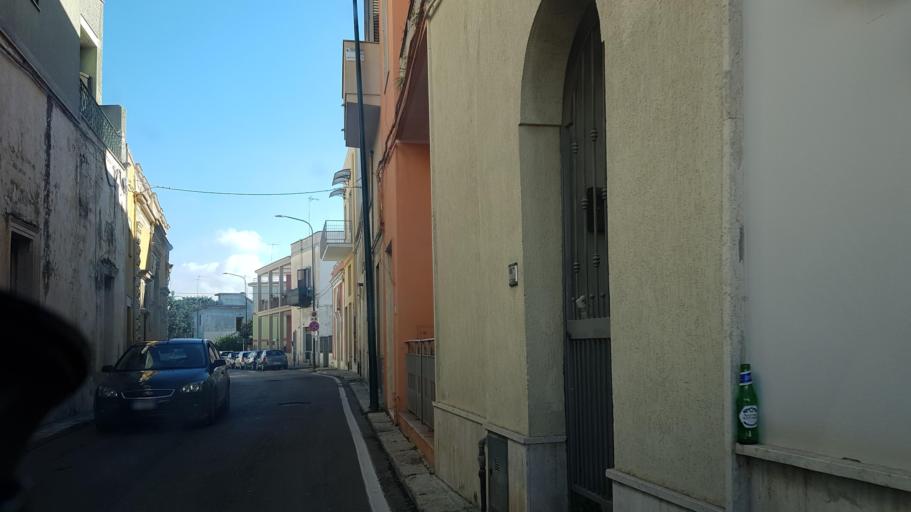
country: IT
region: Apulia
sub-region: Provincia di Lecce
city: Arnesano
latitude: 40.3357
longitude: 18.0929
